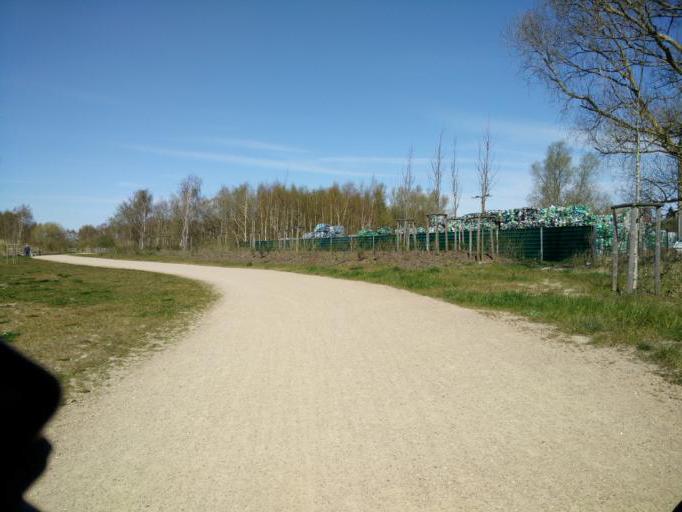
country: DE
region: Mecklenburg-Vorpommern
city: Dierkow-West
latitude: 54.0969
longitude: 12.1538
